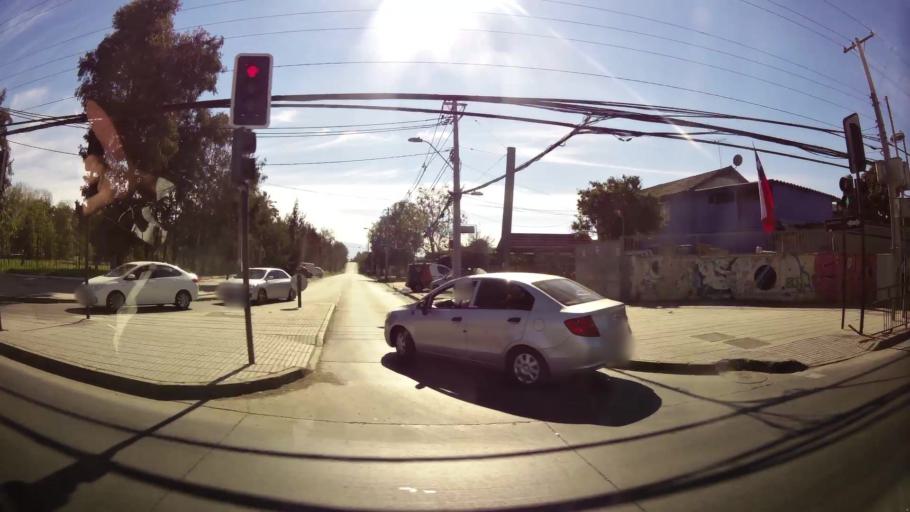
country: CL
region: Santiago Metropolitan
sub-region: Provincia de Santiago
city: Lo Prado
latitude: -33.4972
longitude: -70.7074
